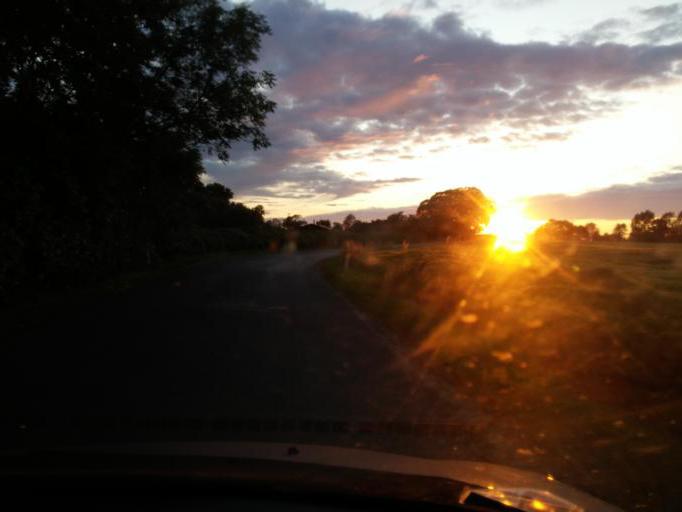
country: DK
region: South Denmark
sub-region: Kerteminde Kommune
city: Kerteminde
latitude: 55.4356
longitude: 10.6062
